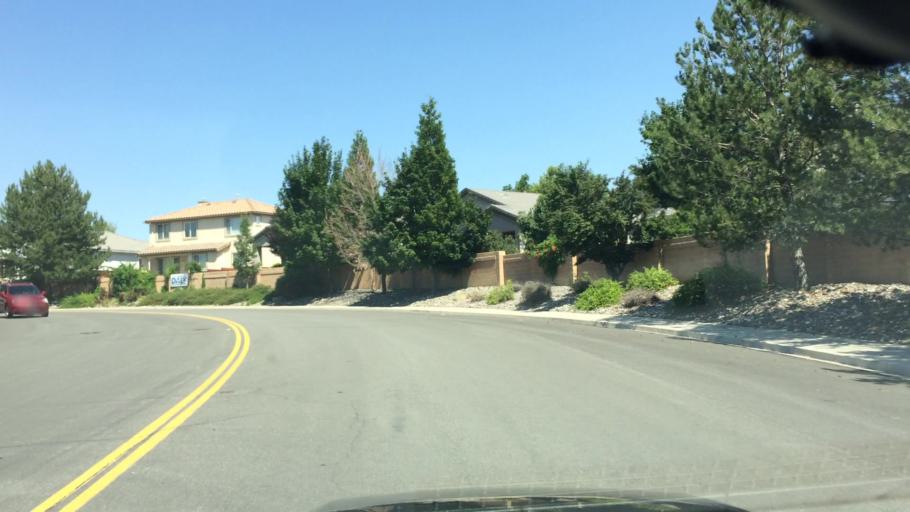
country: US
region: Nevada
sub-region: Washoe County
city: Sparks
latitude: 39.5766
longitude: -119.7178
